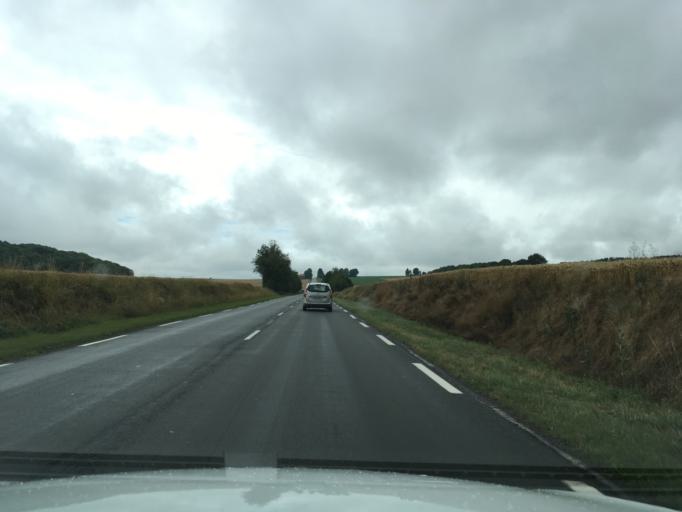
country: FR
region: Picardie
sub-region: Departement de l'Aisne
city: Homblieres
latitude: 49.8435
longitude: 3.4127
